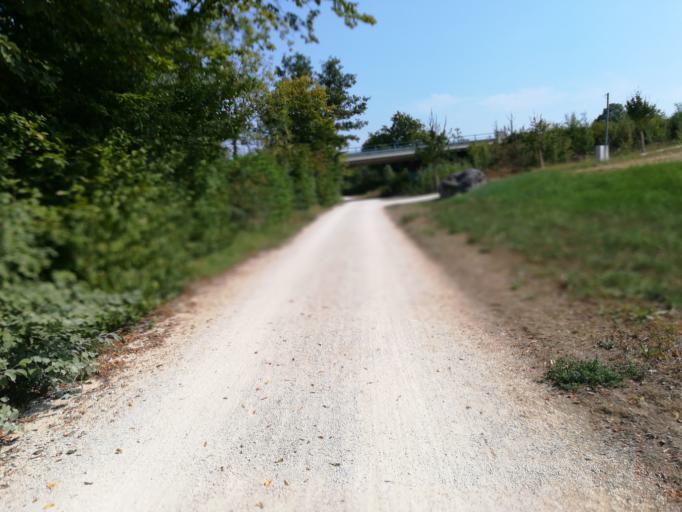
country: DE
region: Baden-Wuerttemberg
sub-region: Freiburg Region
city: Singen
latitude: 47.7758
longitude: 8.8312
